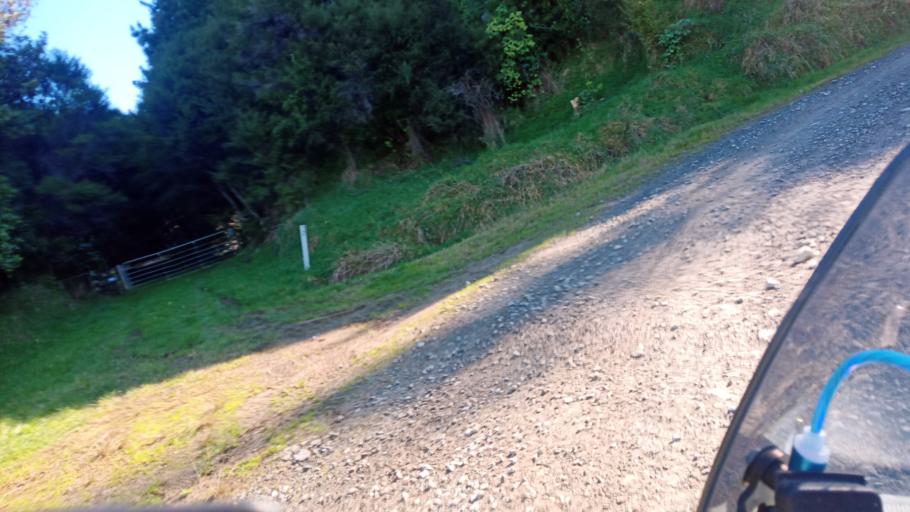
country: NZ
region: Gisborne
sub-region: Gisborne District
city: Gisborne
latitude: -38.2282
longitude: 178.3082
